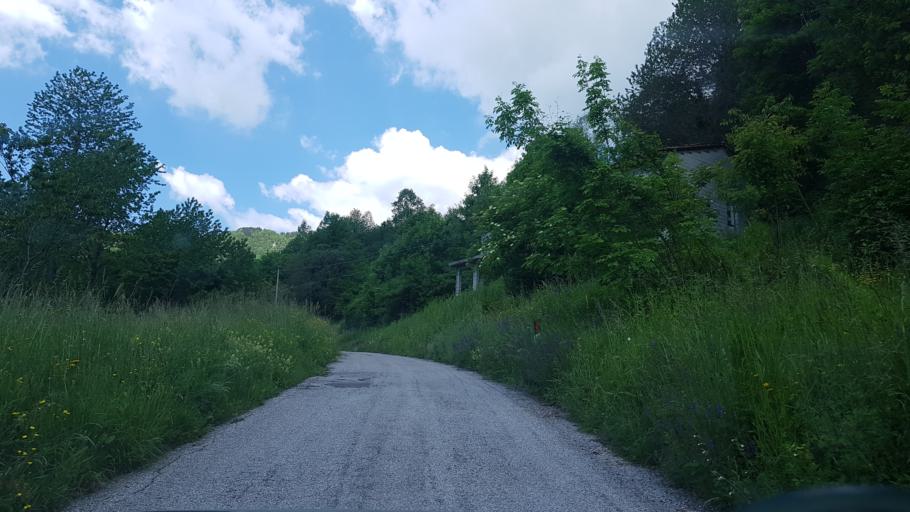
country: IT
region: Friuli Venezia Giulia
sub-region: Provincia di Udine
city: Torreano
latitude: 46.1736
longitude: 13.4330
